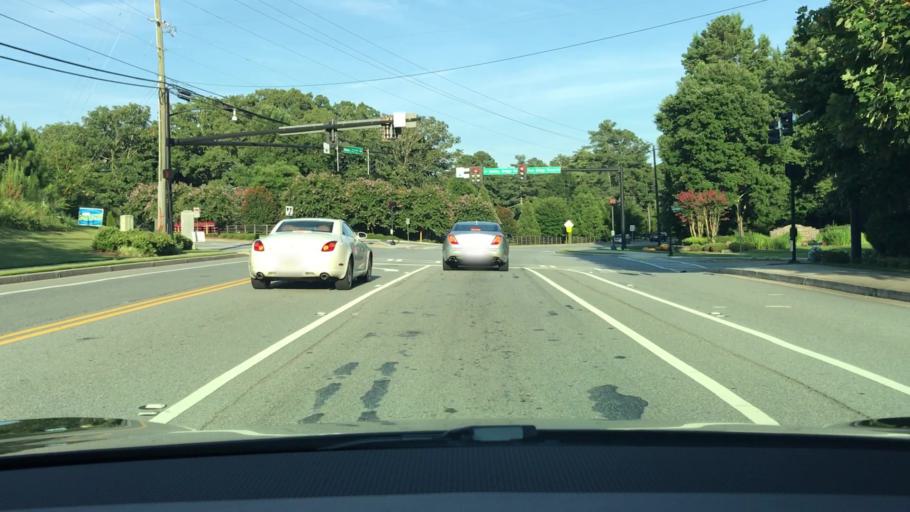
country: US
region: Georgia
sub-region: Fulton County
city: Johns Creek
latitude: 34.0730
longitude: -84.2329
